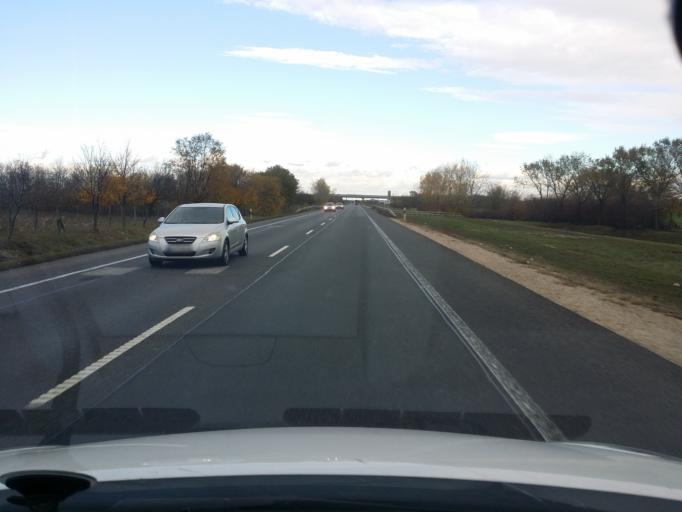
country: HU
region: Gyor-Moson-Sopron
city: Rajka
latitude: 47.9705
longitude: 17.1769
